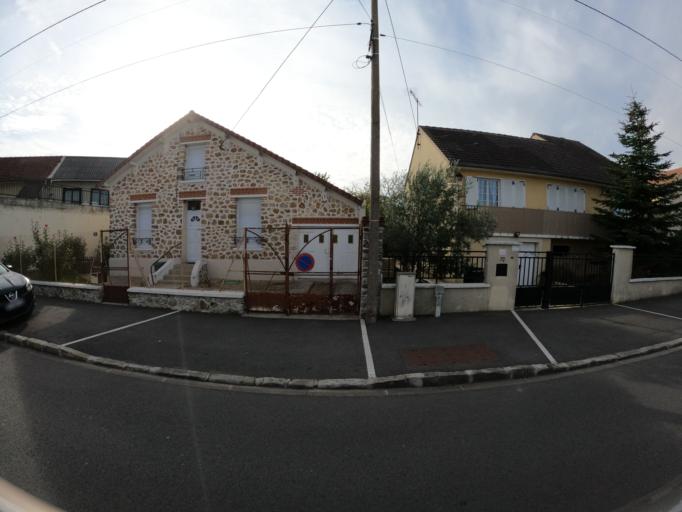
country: FR
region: Ile-de-France
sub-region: Departement de Seine-et-Marne
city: Pontault-Combault
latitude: 48.7932
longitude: 2.6086
